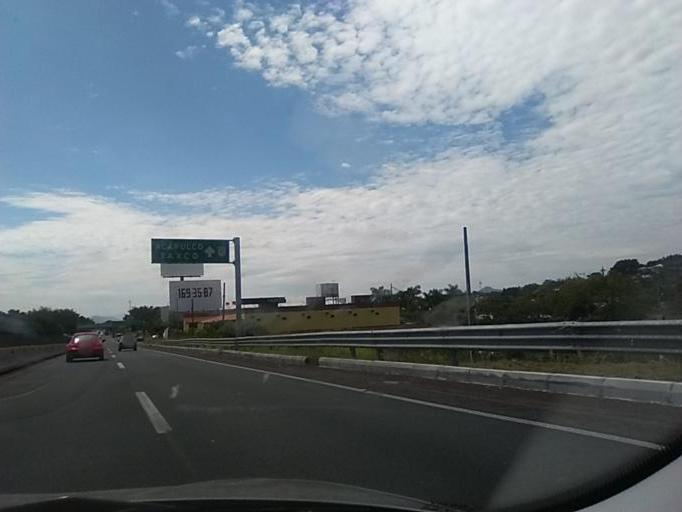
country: MX
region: Morelos
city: Temixco
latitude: 18.8630
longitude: -99.2211
